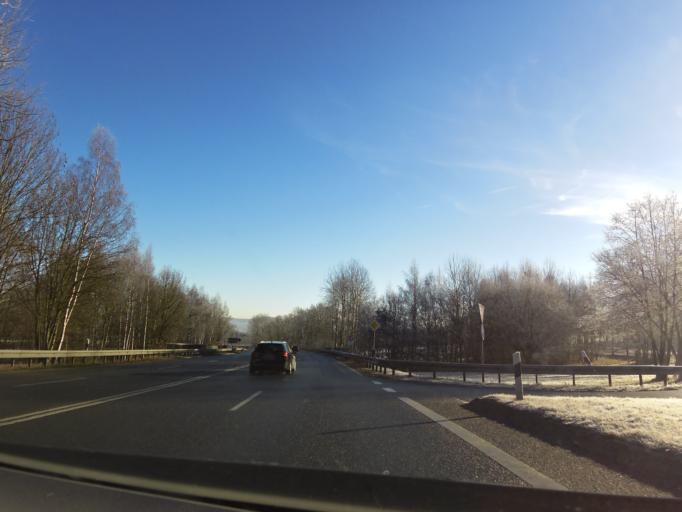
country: DE
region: Bavaria
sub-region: Upper Franconia
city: Marktredwitz
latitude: 50.0109
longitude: 12.0590
